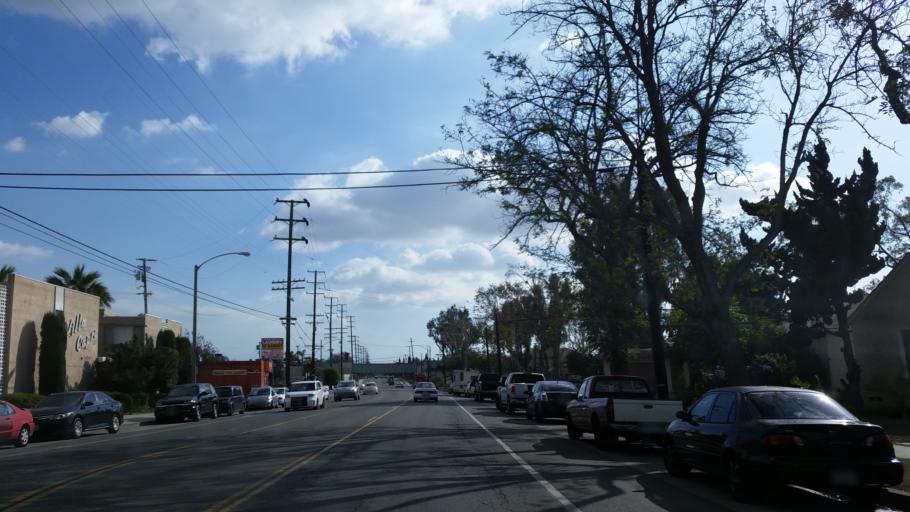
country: US
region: California
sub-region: Los Angeles County
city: Paramount
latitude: 33.8516
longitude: -118.1773
